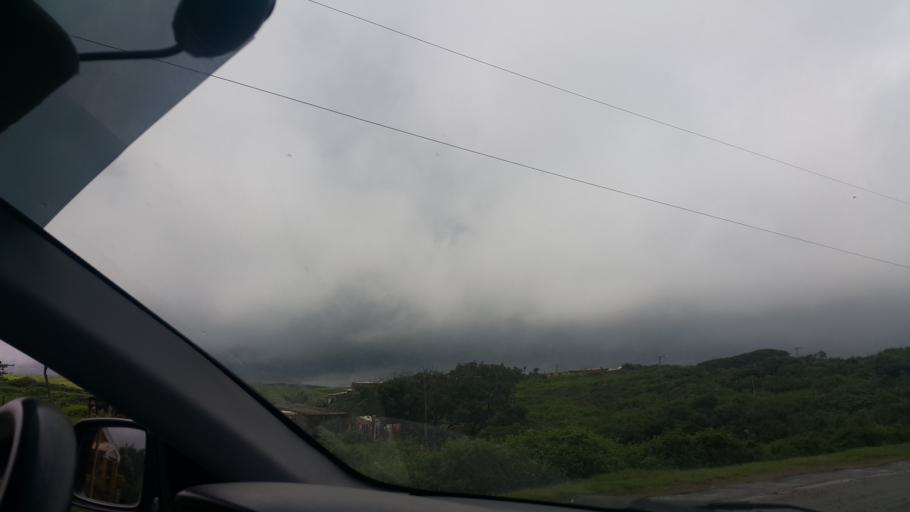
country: NI
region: Managua
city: El Crucero
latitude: 11.9467
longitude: -86.2999
